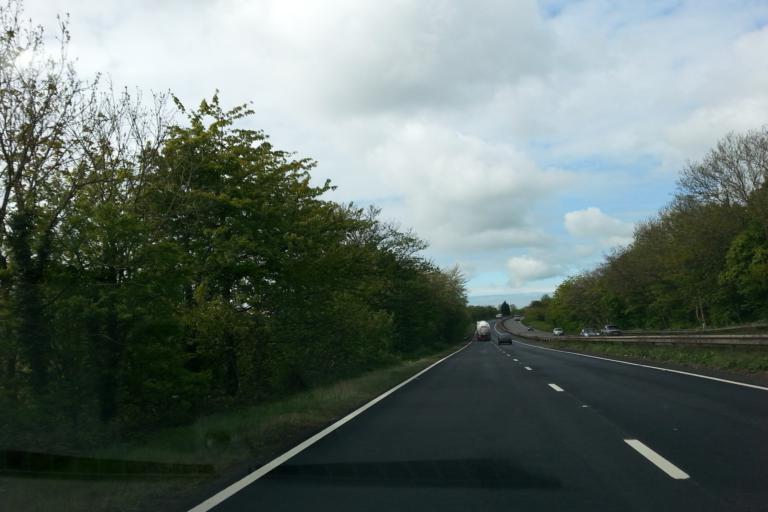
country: GB
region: England
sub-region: Staffordshire
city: Burton upon Trent
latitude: 52.8186
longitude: -1.6413
